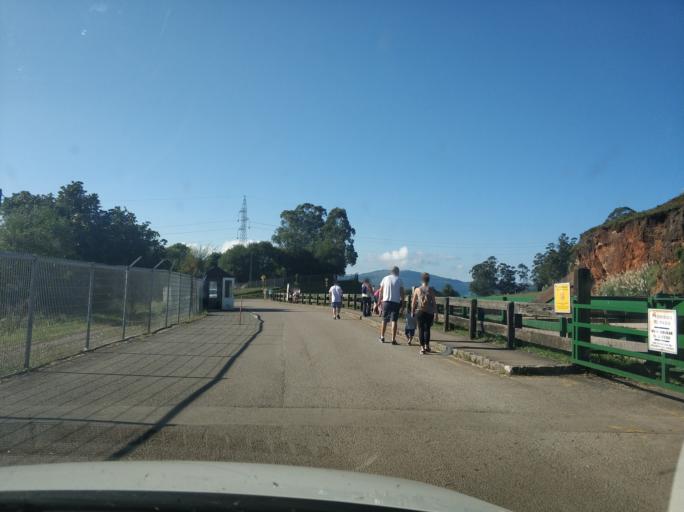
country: ES
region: Cantabria
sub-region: Provincia de Cantabria
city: Penagos
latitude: 43.3495
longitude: -3.8427
